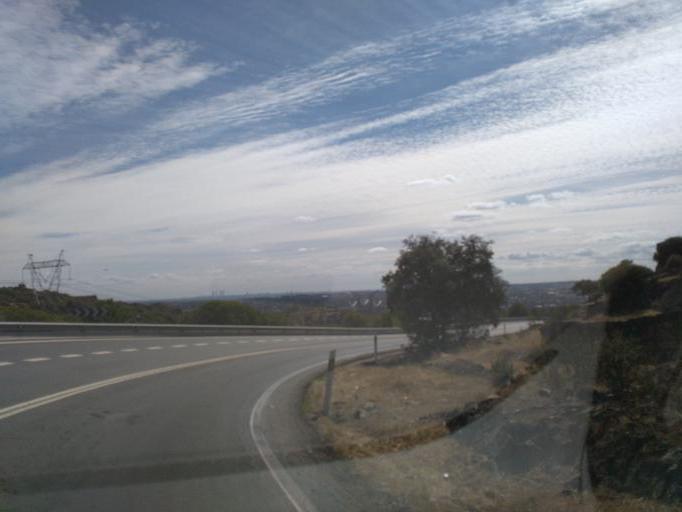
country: ES
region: Madrid
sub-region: Provincia de Madrid
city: Torrelodones
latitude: 40.5528
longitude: -3.9586
